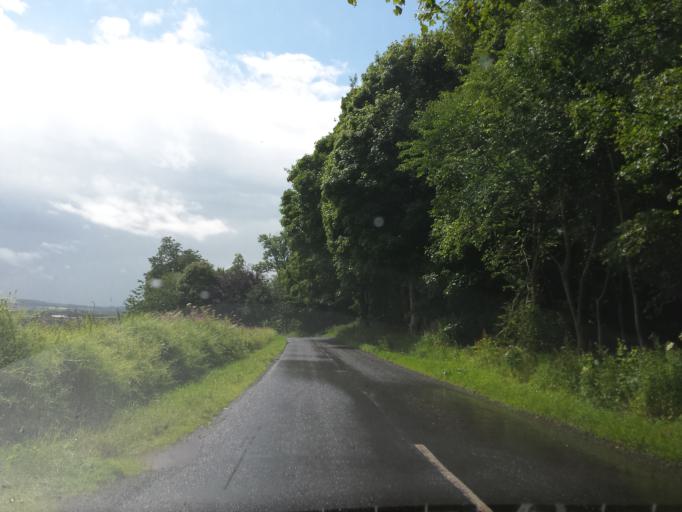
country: GB
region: Scotland
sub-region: The Scottish Borders
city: Saint Boswells
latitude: 55.5837
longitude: -2.6399
